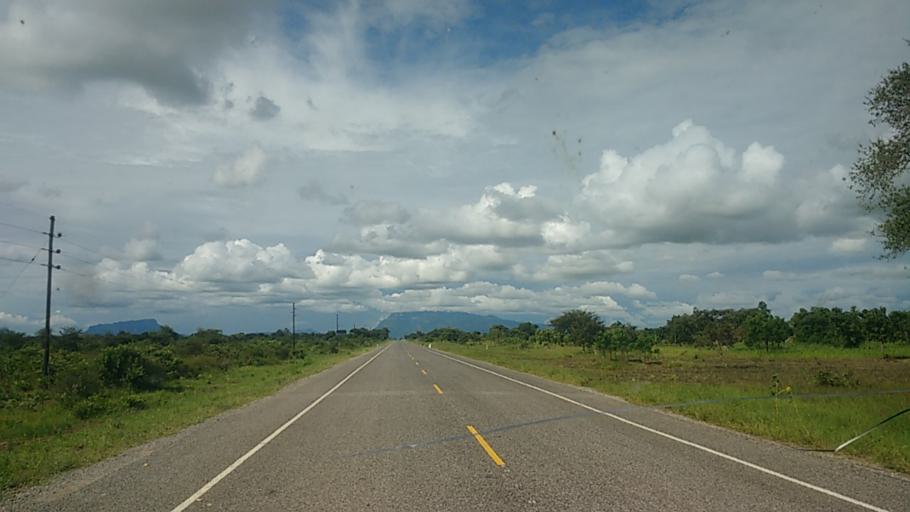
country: UG
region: Eastern Region
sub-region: Katakwi District
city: Katakwi
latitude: 1.9364
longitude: 34.0725
